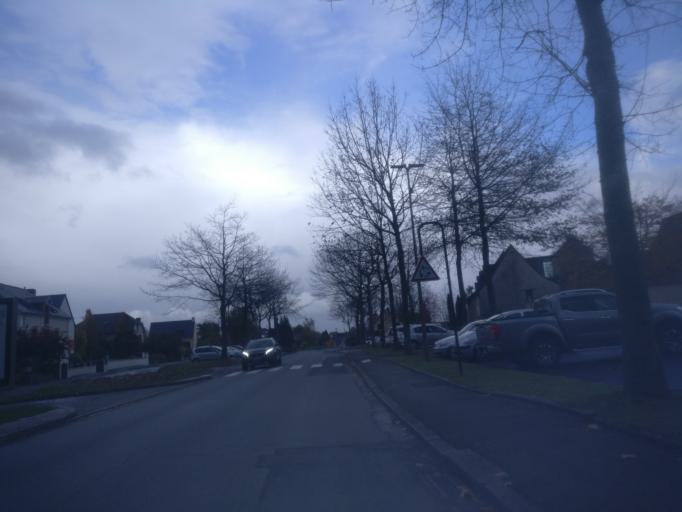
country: FR
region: Brittany
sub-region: Departement d'Ille-et-Vilaine
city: Breal-sous-Montfort
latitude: 48.0480
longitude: -1.8633
